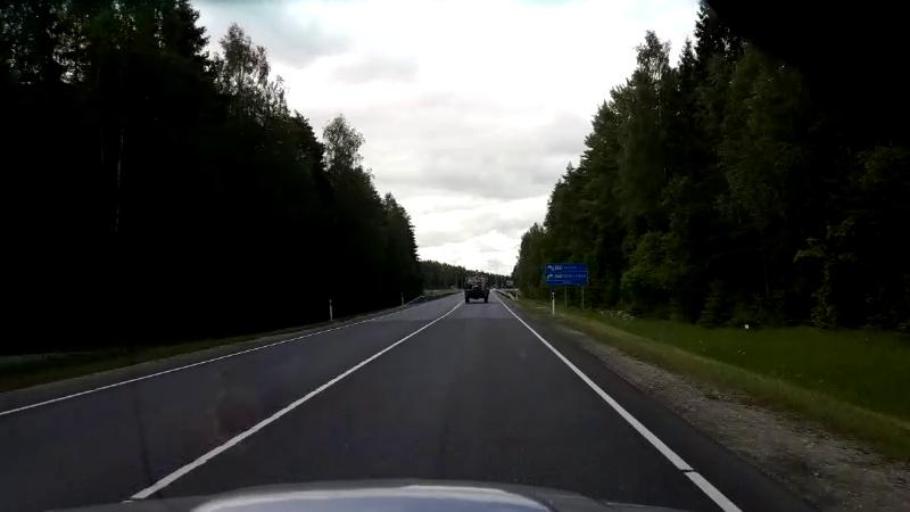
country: EE
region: Raplamaa
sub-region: Maerjamaa vald
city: Marjamaa
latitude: 58.8982
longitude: 24.4555
